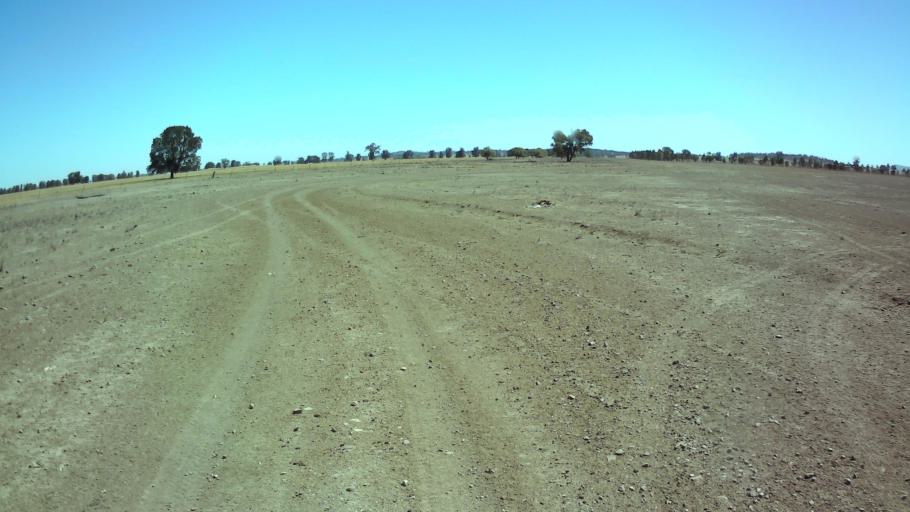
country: AU
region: New South Wales
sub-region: Forbes
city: Forbes
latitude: -33.7246
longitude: 147.6655
